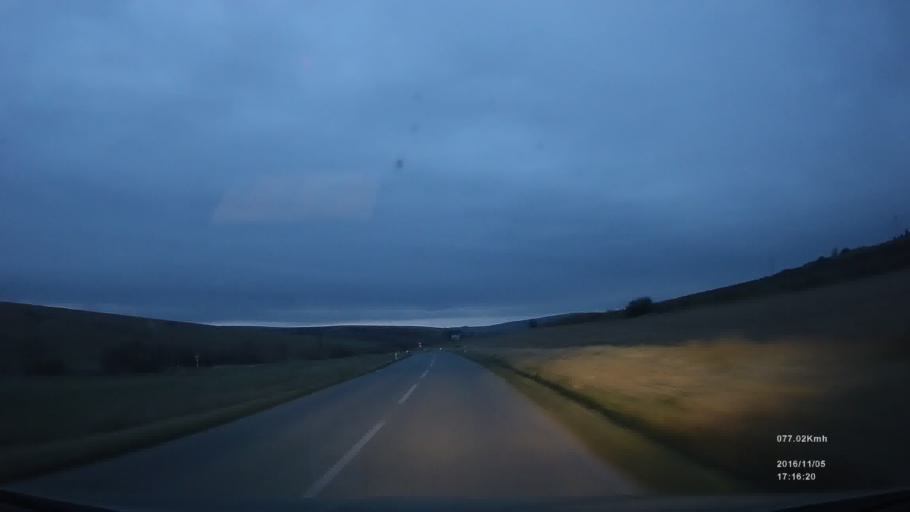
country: SK
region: Presovsky
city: Lubica
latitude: 49.0996
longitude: 20.4395
